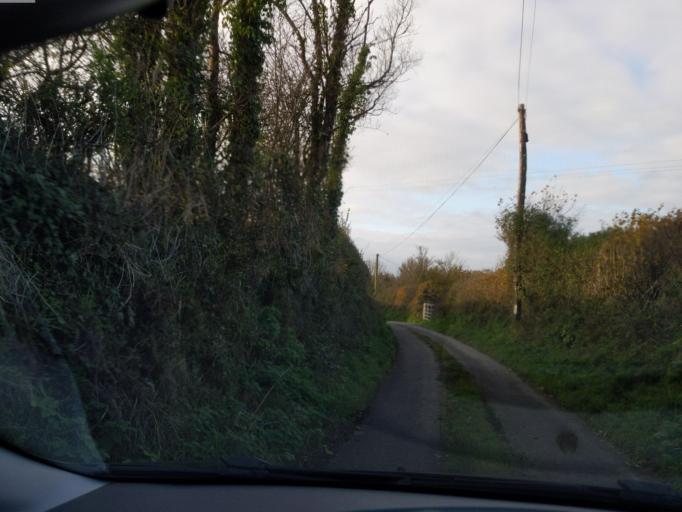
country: GB
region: England
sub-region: Cornwall
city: Wadebridge
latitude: 50.5071
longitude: -4.8010
